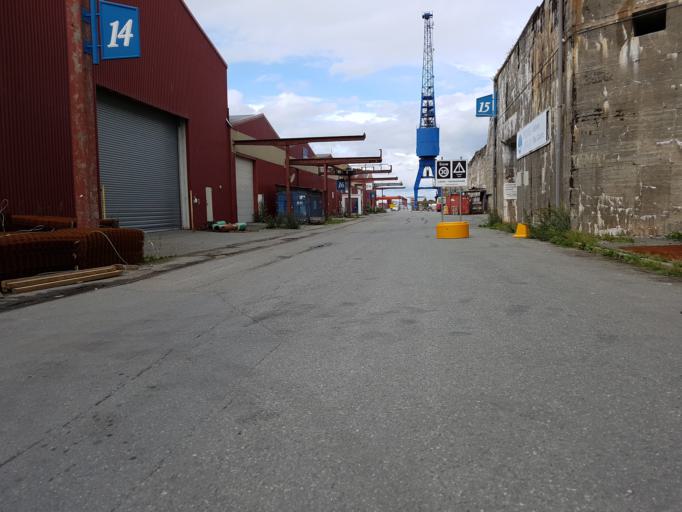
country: NO
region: Sor-Trondelag
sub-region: Trondheim
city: Trondheim
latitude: 63.4404
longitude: 10.4156
